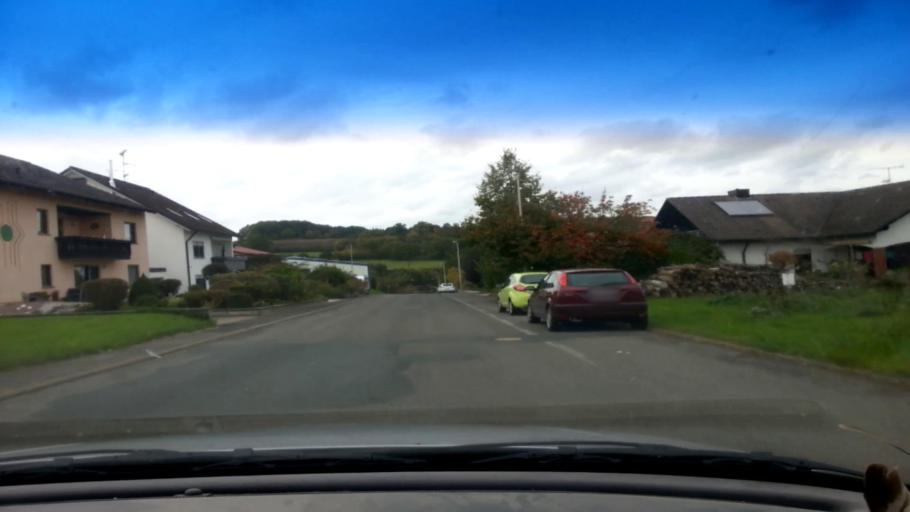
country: DE
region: Bavaria
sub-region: Upper Franconia
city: Gerach
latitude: 50.0306
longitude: 10.8110
